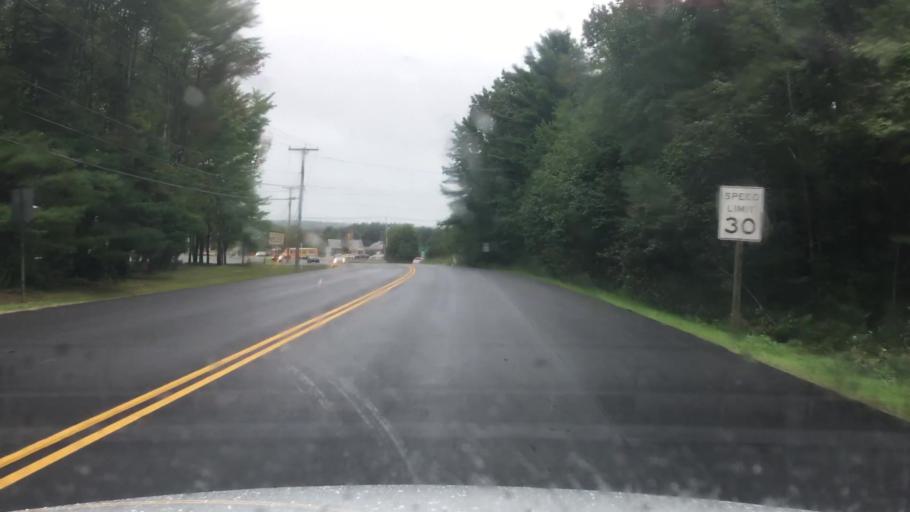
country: US
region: Maine
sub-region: Penobscot County
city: Hampden
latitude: 44.7557
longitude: -68.8419
